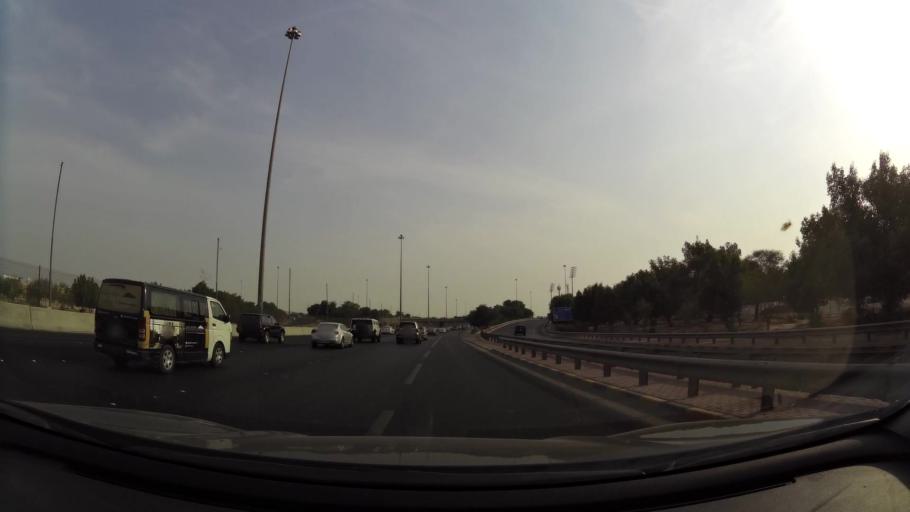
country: KW
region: Al Farwaniyah
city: Janub as Surrah
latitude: 29.2869
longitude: 47.9842
